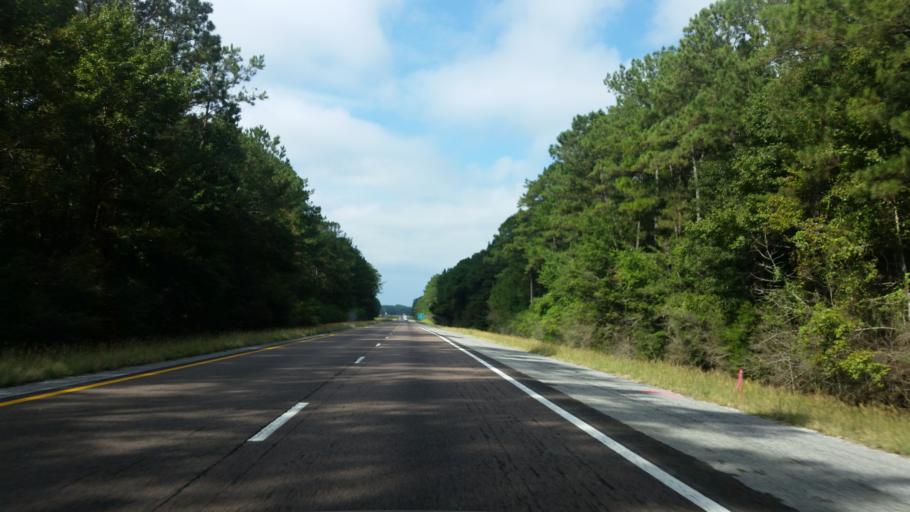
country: US
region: Alabama
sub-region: Baldwin County
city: Bay Minette
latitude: 30.9576
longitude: -87.8057
